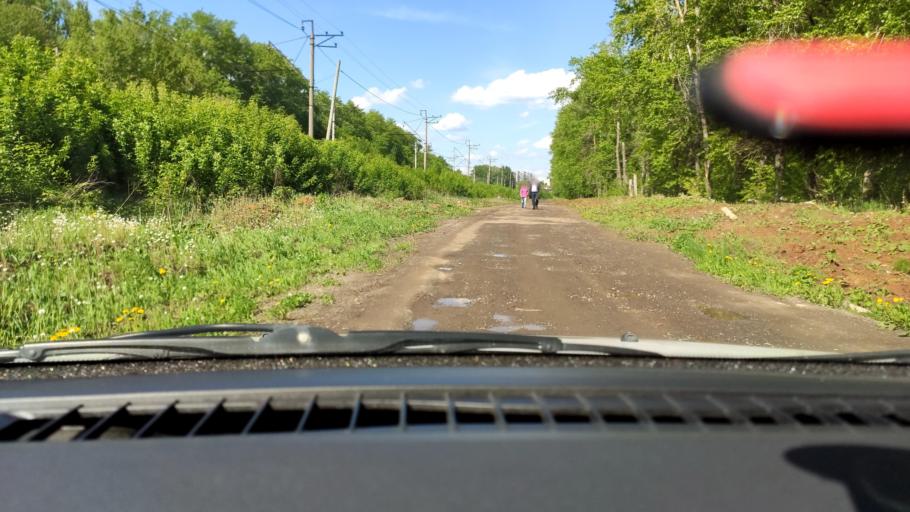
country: RU
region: Perm
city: Perm
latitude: 57.9637
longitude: 56.2056
